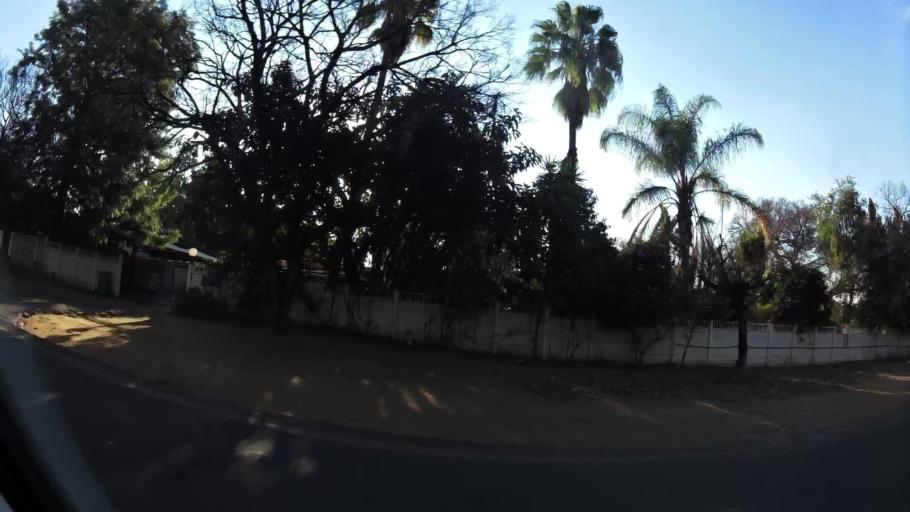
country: ZA
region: North-West
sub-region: Bojanala Platinum District Municipality
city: Rustenburg
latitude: -25.6780
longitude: 27.2306
